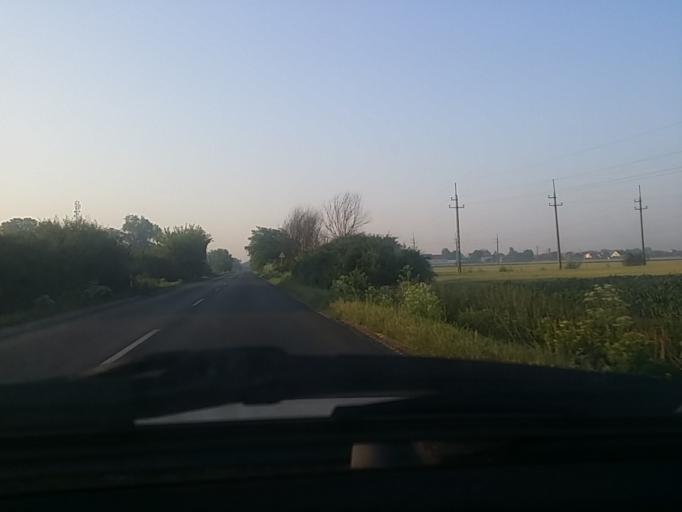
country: HU
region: Pest
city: Nagykata
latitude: 47.4306
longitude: 19.7322
